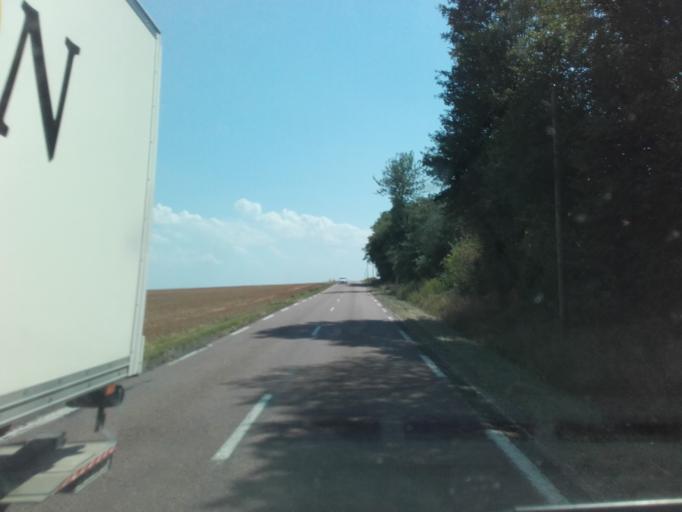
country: FR
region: Bourgogne
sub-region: Departement de l'Yonne
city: Joux-la-Ville
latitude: 47.6976
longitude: 3.8613
